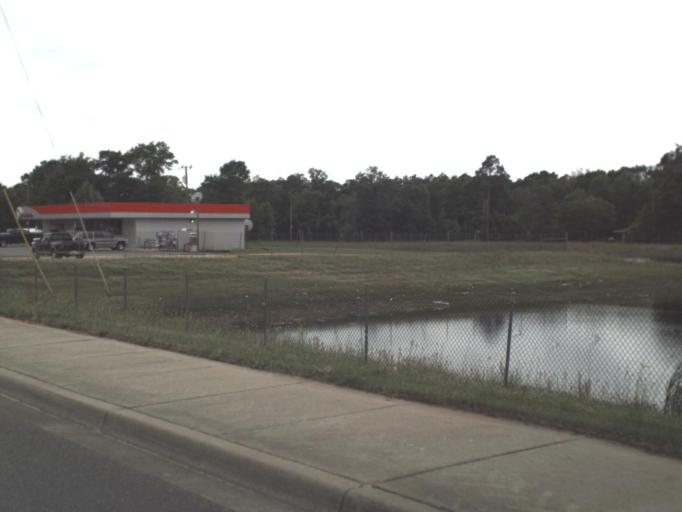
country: US
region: Florida
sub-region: Santa Rosa County
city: Point Baker
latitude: 30.6853
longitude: -87.0540
